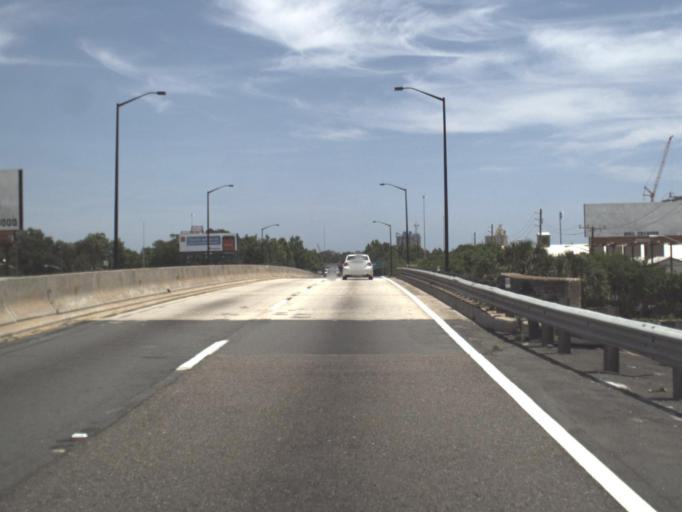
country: US
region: Florida
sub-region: Duval County
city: Jacksonville
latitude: 30.3284
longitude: -81.6432
